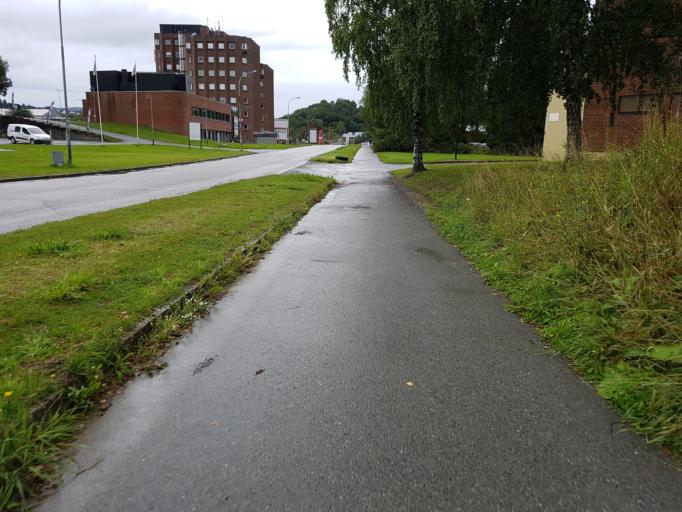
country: NO
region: Sor-Trondelag
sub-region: Trondheim
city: Trondheim
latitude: 63.3904
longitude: 10.4044
